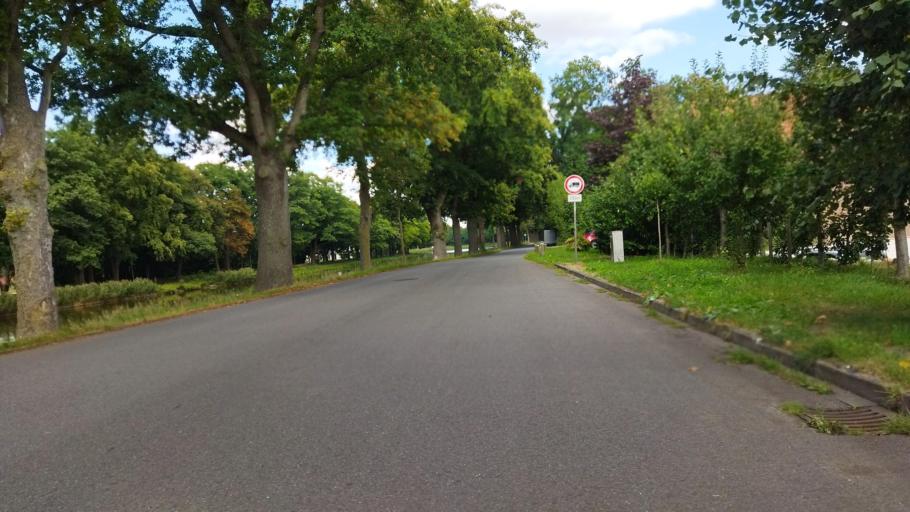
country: DE
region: Lower Saxony
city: Lingen
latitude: 52.5057
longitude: 7.3096
